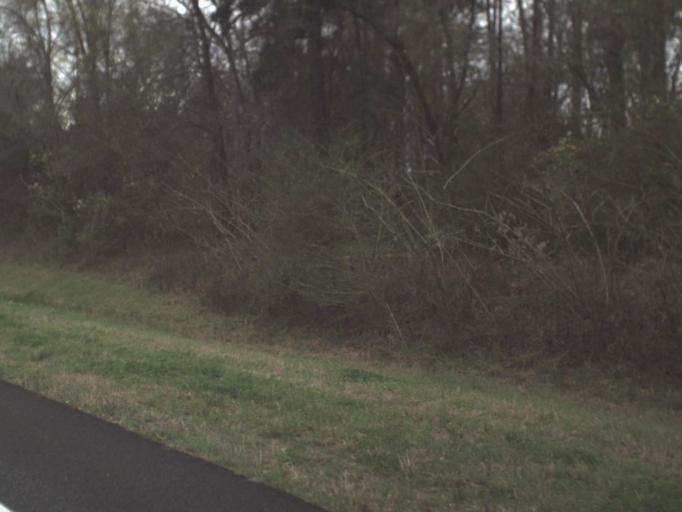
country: US
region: Florida
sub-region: Leon County
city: Tallahassee
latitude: 30.6355
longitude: -84.1693
